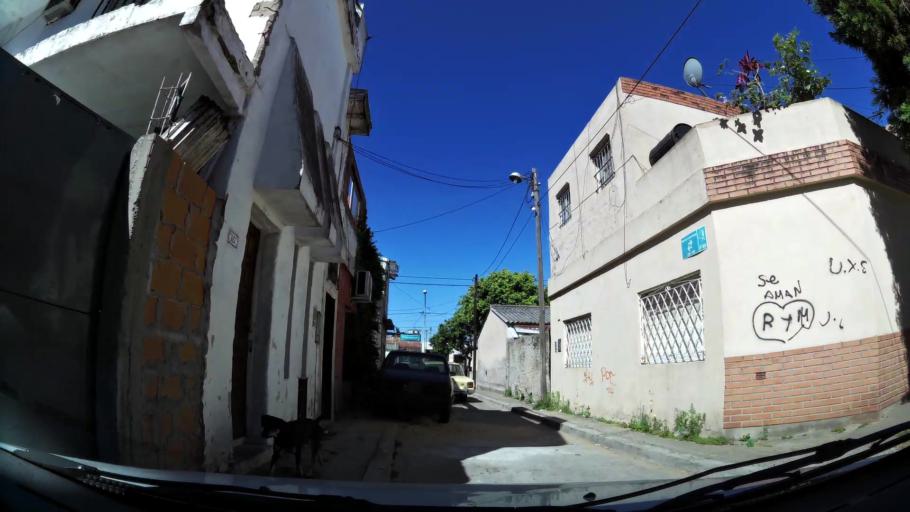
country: AR
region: Buenos Aires
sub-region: Partido de General San Martin
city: General San Martin
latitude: -34.5465
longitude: -58.5298
